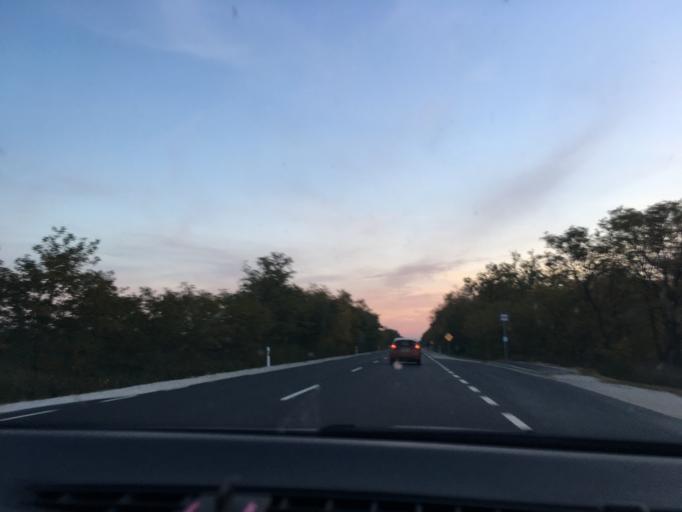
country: HU
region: Hajdu-Bihar
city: Hajduhadhaz
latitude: 47.6170
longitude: 21.6585
